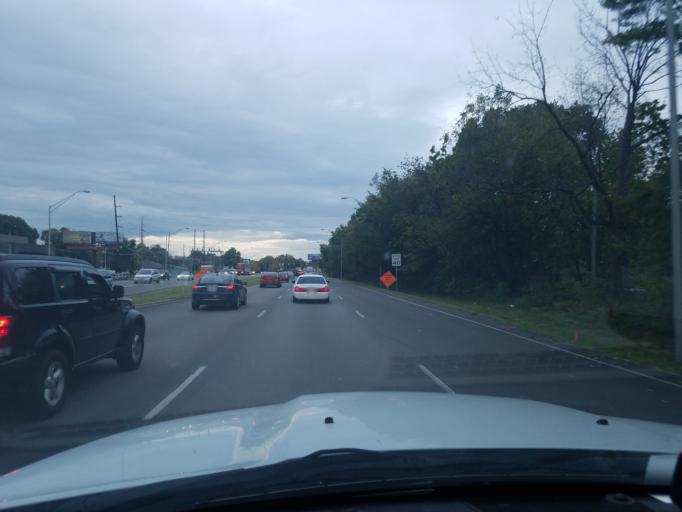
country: US
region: Indiana
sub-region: Vanderburgh County
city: Evansville
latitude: 37.9734
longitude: -87.5440
